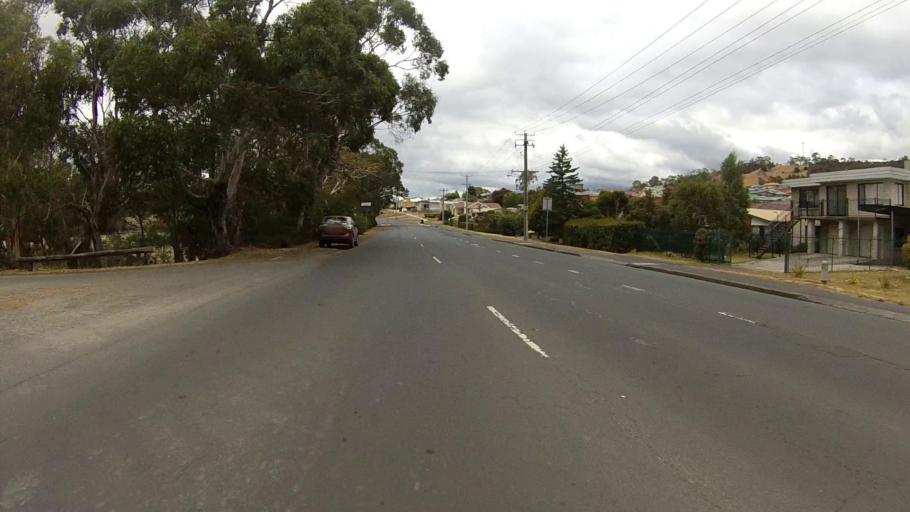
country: AU
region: Tasmania
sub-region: Glenorchy
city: Austins Ferry
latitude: -42.7718
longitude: 147.2476
